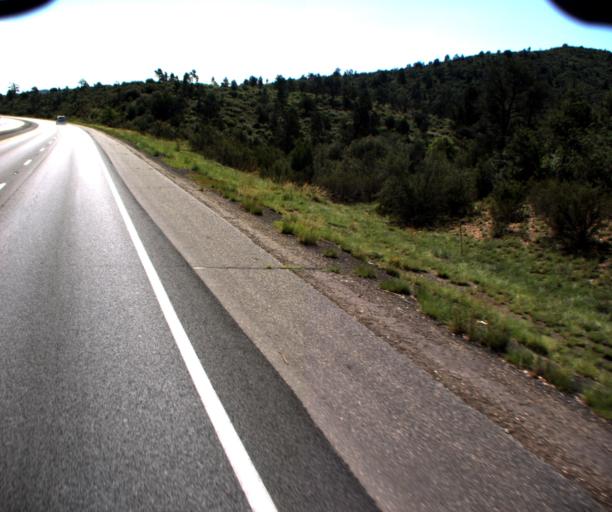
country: US
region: Arizona
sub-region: Yavapai County
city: Prescott
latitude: 34.5490
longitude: -112.3929
